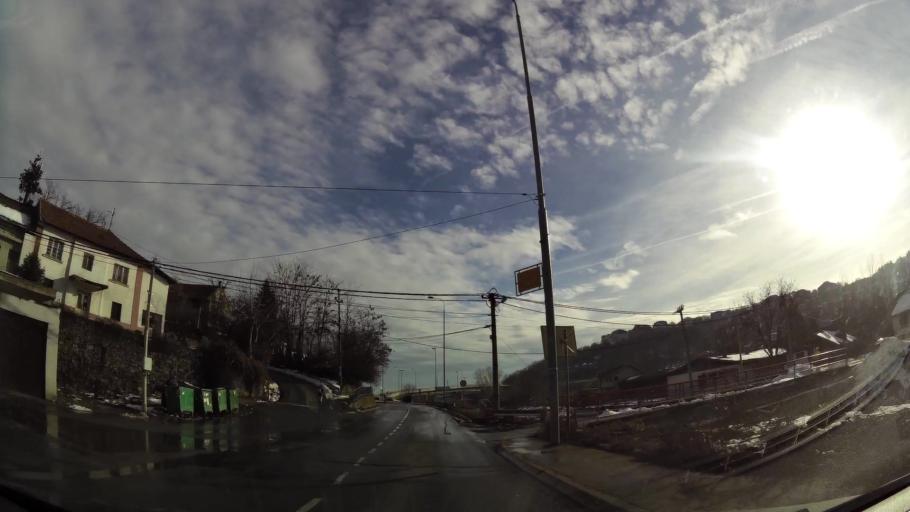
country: RS
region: Central Serbia
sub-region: Belgrade
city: Rakovica
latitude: 44.7328
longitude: 20.4319
